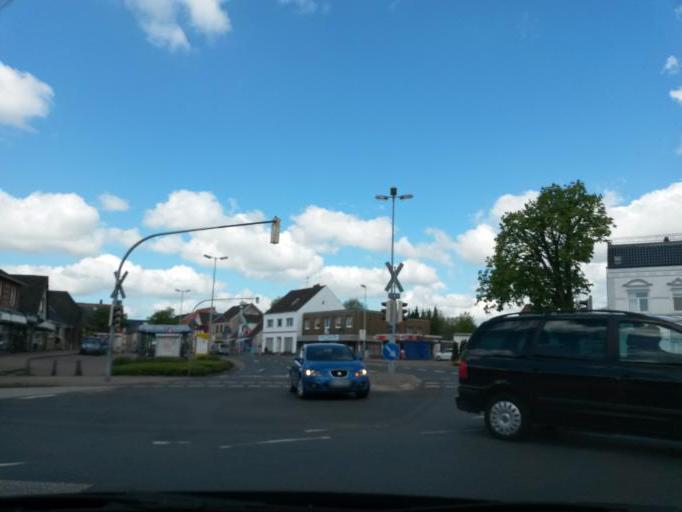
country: DE
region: Schleswig-Holstein
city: Uetersen
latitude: 53.6797
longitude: 9.6772
